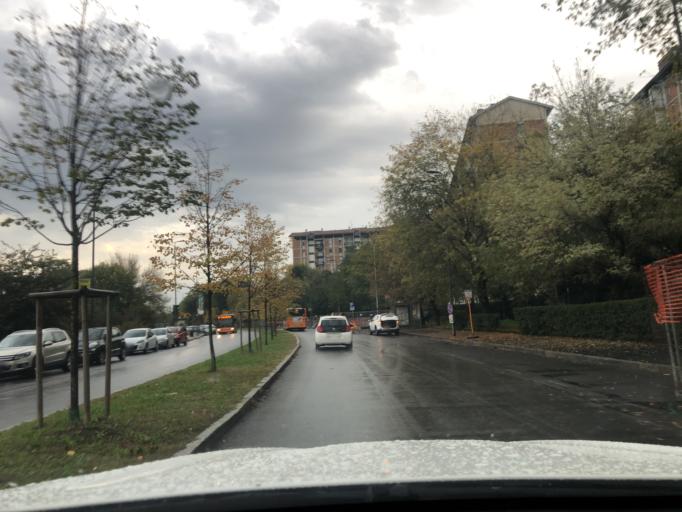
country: IT
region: Lombardy
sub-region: Citta metropolitana di Milano
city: Baranzate
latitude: 45.4936
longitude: 9.1195
